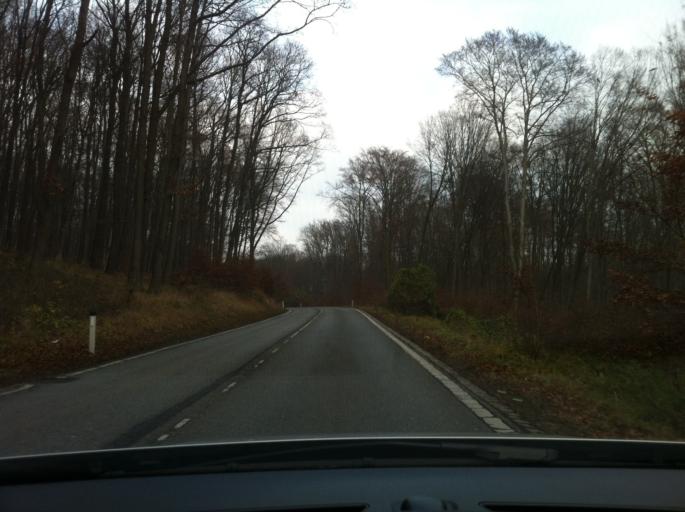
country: AT
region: Lower Austria
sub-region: Politischer Bezirk Wien-Umgebung
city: Purkersdorf
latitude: 48.2221
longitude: 16.2524
